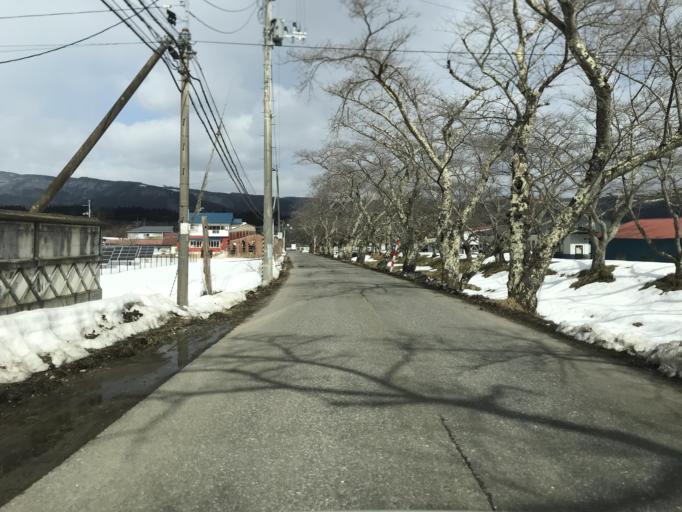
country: JP
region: Miyagi
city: Furukawa
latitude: 38.7295
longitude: 140.7648
